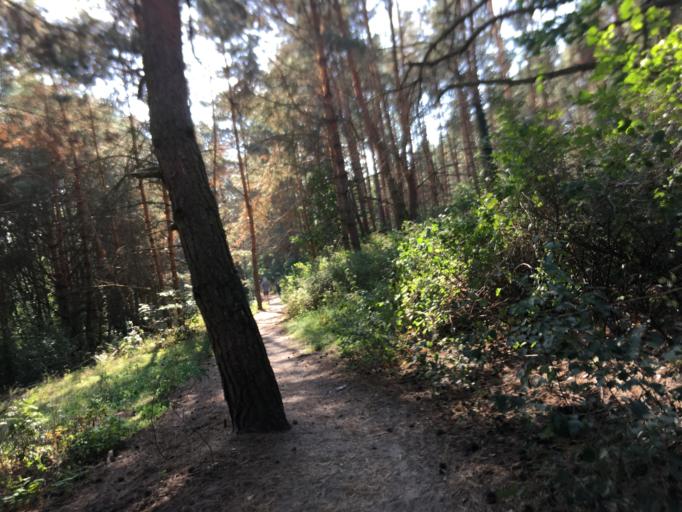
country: DE
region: Berlin
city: Friedrichshagen
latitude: 52.4730
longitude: 13.6207
